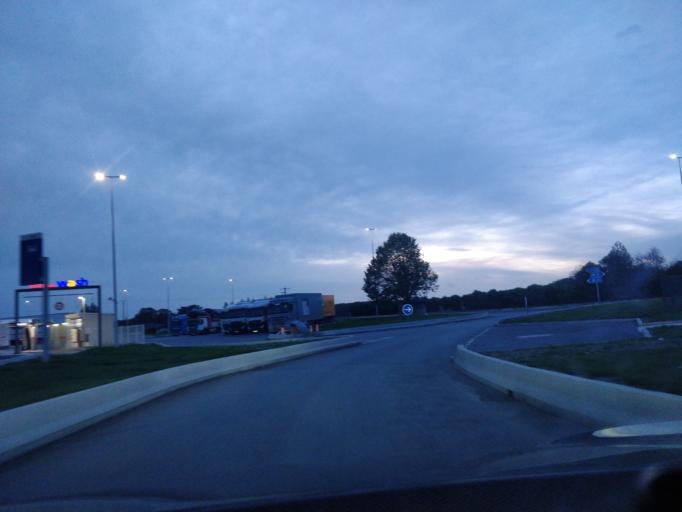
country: FR
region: Ile-de-France
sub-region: Departement de l'Essonne
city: Fontenay-les-Briis
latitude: 48.6370
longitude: 2.1467
